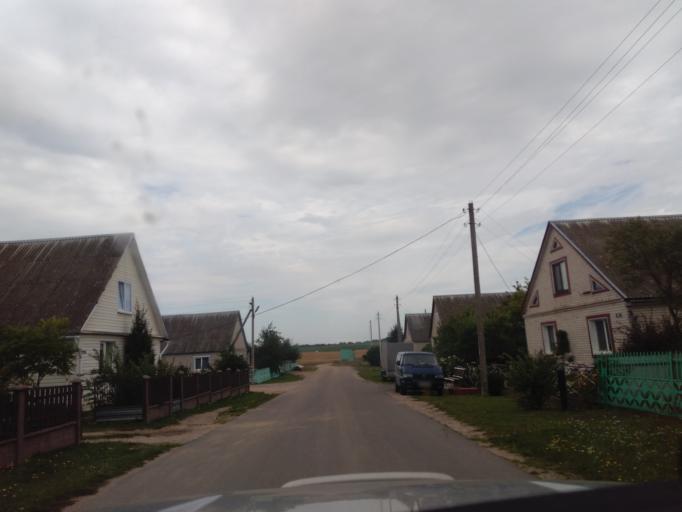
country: BY
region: Minsk
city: Kapyl'
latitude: 53.1577
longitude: 27.0674
